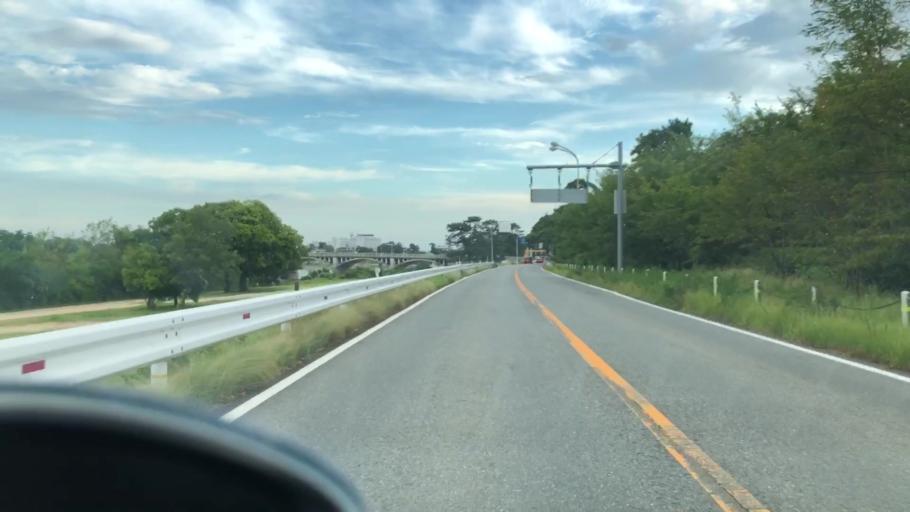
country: JP
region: Hyogo
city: Amagasaki
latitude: 34.7348
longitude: 135.3794
